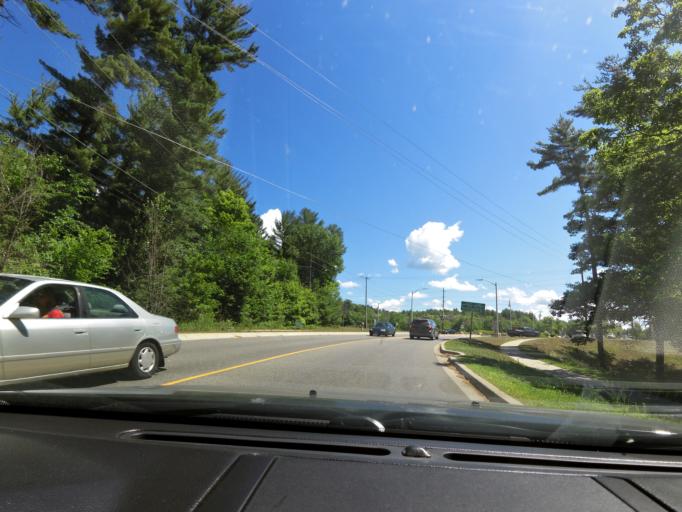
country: CA
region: Ontario
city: Bracebridge
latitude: 45.0503
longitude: -79.2968
